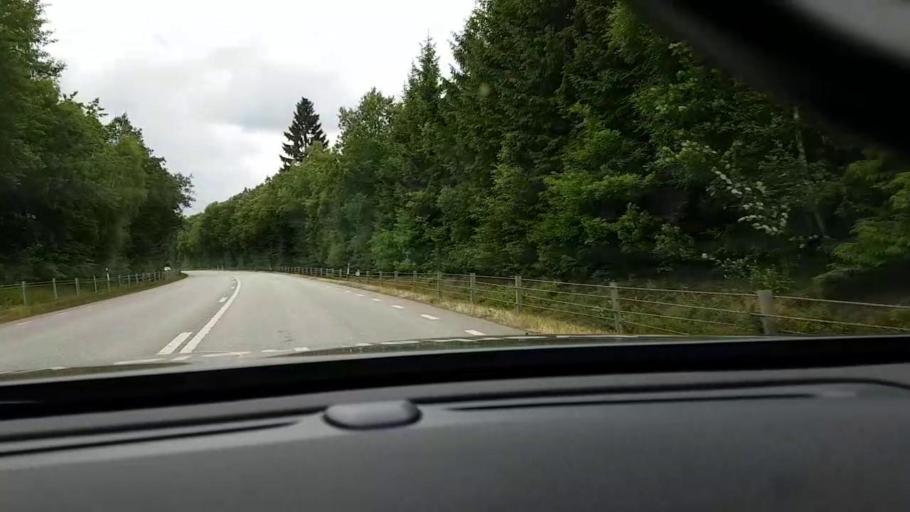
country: SE
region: Skane
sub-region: Horby Kommun
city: Hoerby
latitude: 55.8667
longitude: 13.6383
